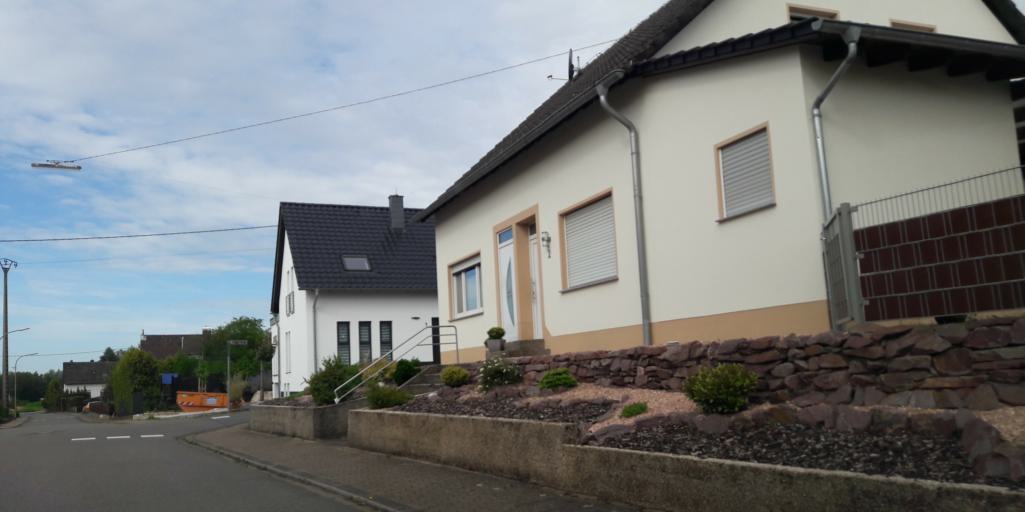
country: DE
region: Saarland
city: Schwalbach
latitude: 49.3089
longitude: 6.8493
